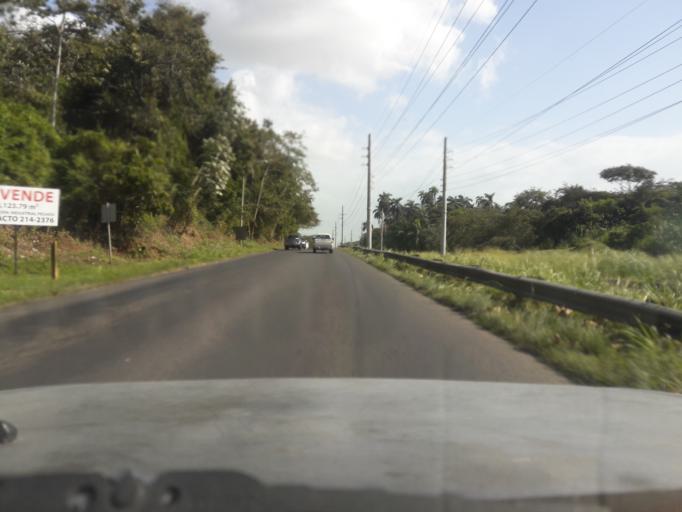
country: PA
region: Panama
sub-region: Distrito de Panama
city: Ancon
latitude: 8.9911
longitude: -79.5798
